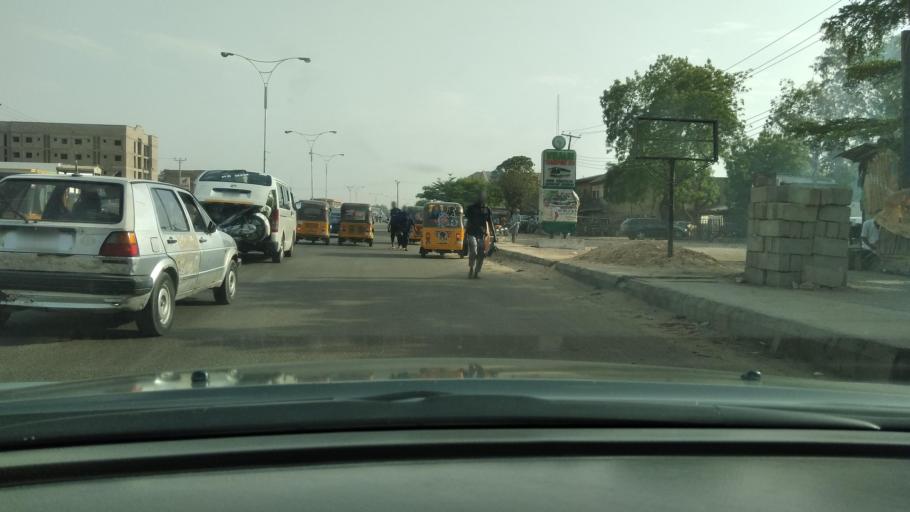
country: NG
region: Kano
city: Kano
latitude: 11.9440
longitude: 8.5652
